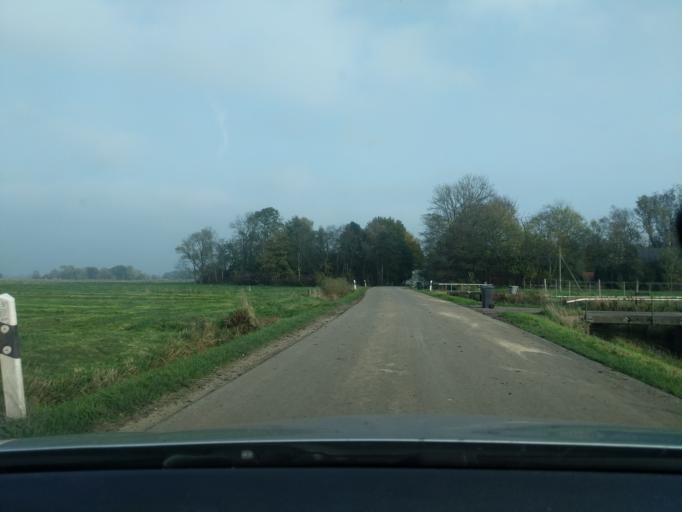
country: DE
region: Lower Saxony
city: Nordleda
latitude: 53.7282
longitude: 8.8447
